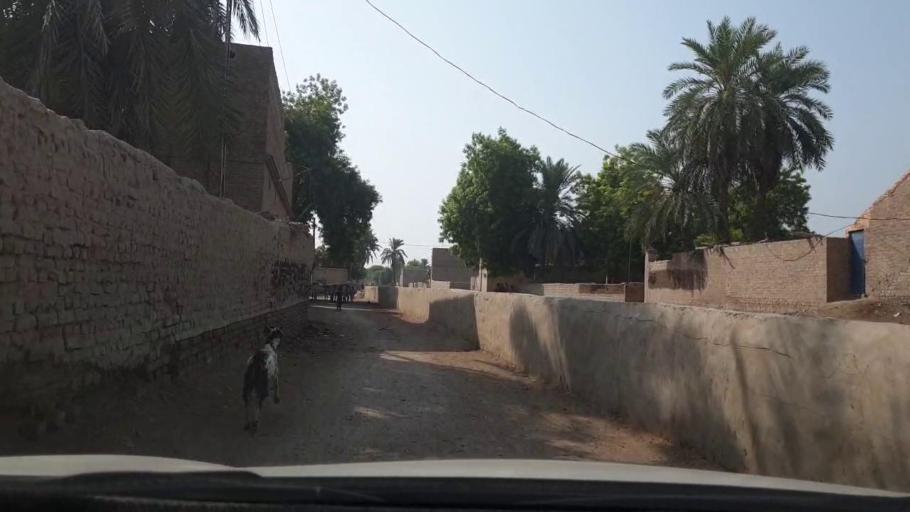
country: PK
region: Sindh
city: Larkana
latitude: 27.4653
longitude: 68.2434
